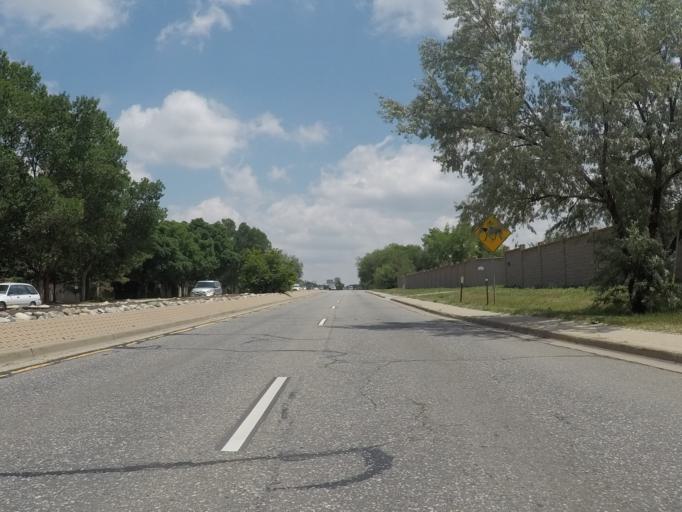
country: US
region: Colorado
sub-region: Arapahoe County
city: Greenwood Village
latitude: 39.6242
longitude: -104.9533
